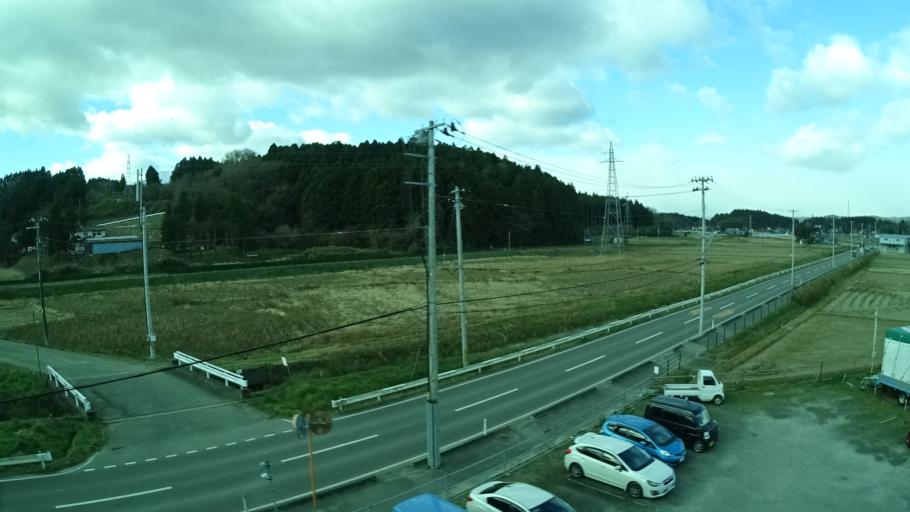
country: JP
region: Miyagi
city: Iwanuma
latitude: 38.0730
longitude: 140.8541
